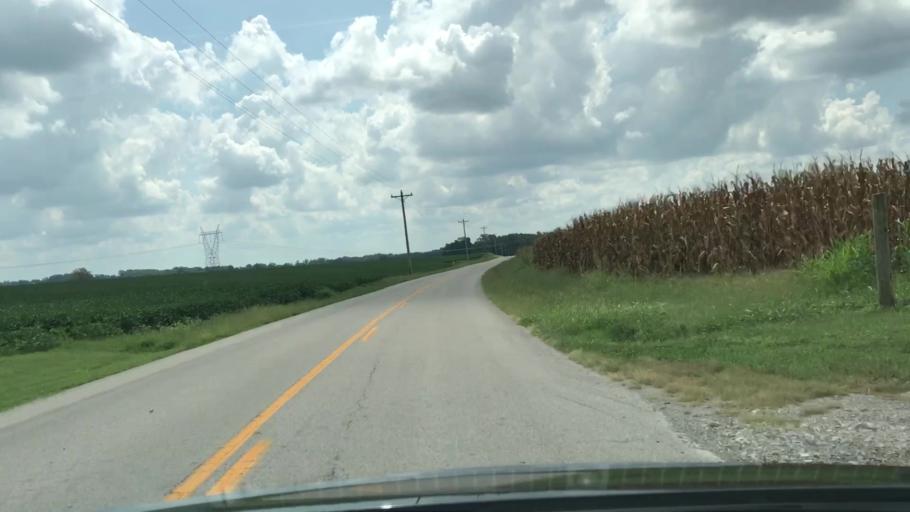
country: US
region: Kentucky
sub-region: Todd County
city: Elkton
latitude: 36.7784
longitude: -87.1202
